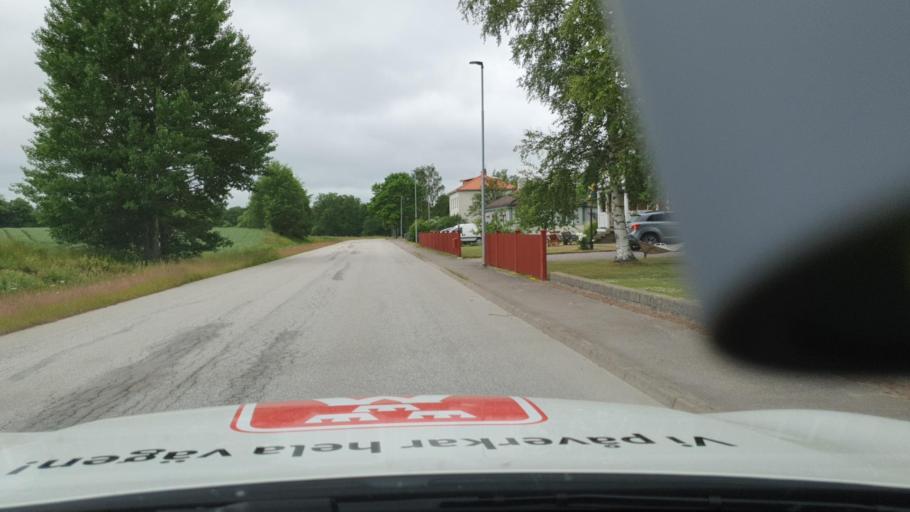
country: SE
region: Vaestra Goetaland
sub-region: Tibro Kommun
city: Tibro
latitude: 58.4039
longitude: 14.1435
